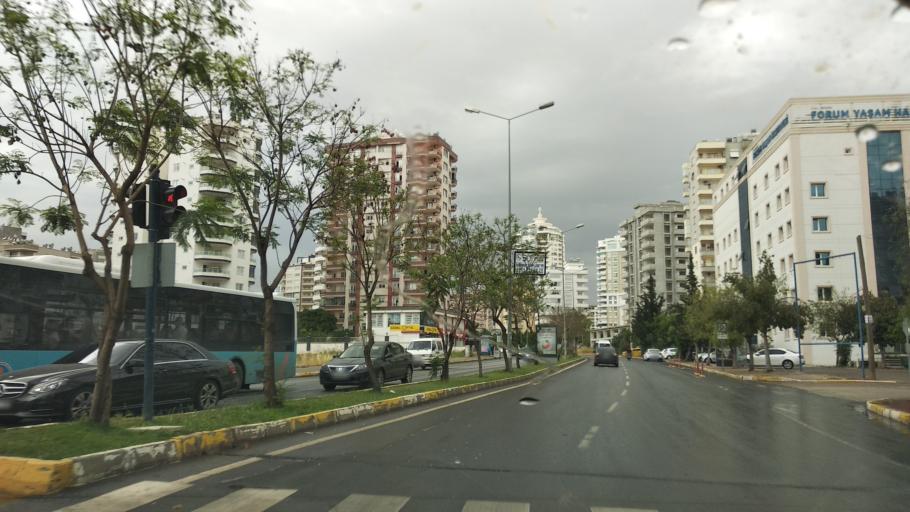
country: TR
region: Mersin
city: Mercin
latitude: 36.7888
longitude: 34.5879
